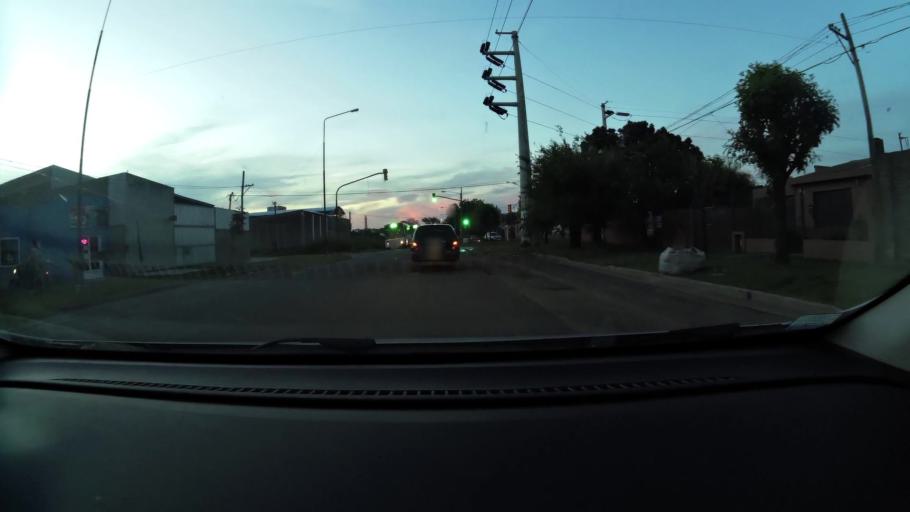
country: AR
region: Buenos Aires
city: San Nicolas de los Arroyos
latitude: -33.3522
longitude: -60.2139
